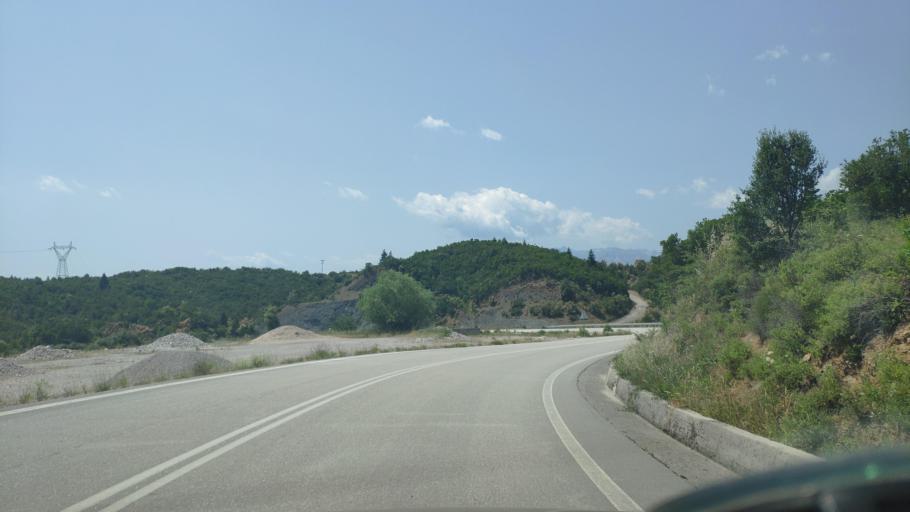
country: GR
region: Epirus
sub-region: Nomos Artas
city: Ano Kalentini
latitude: 39.2860
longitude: 21.3165
